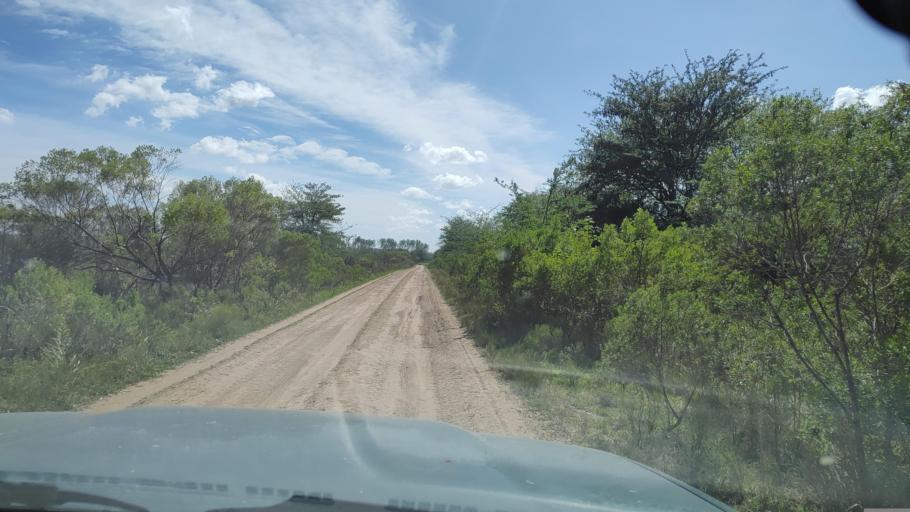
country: AR
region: Buenos Aires
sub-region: Partido de Lujan
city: Lujan
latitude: -34.5188
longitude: -59.1642
